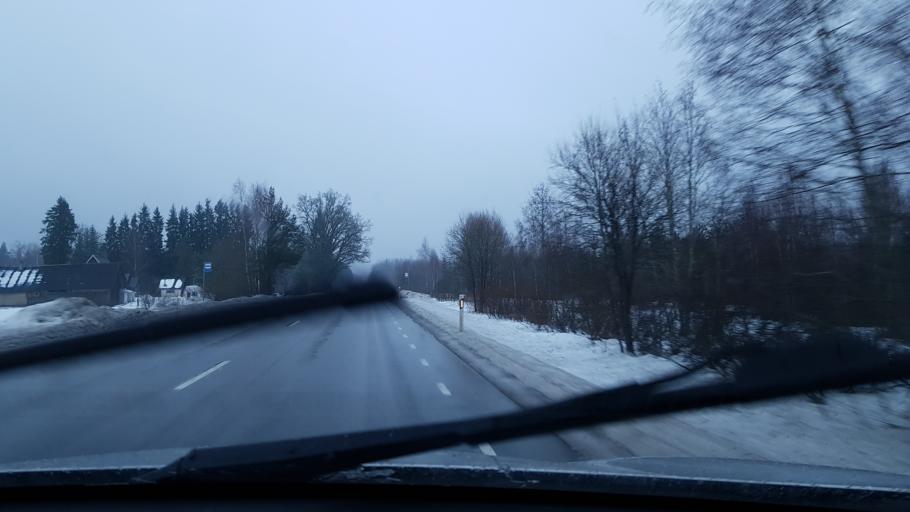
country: EE
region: Paernumaa
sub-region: Vaendra vald (alev)
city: Vandra
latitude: 58.8102
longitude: 25.1932
